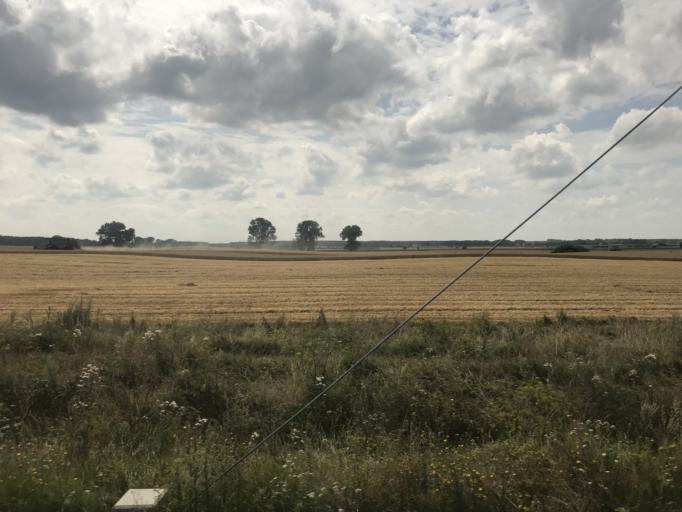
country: PL
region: Greater Poland Voivodeship
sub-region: Powiat poznanski
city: Pobiedziska
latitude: 52.4890
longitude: 17.3469
